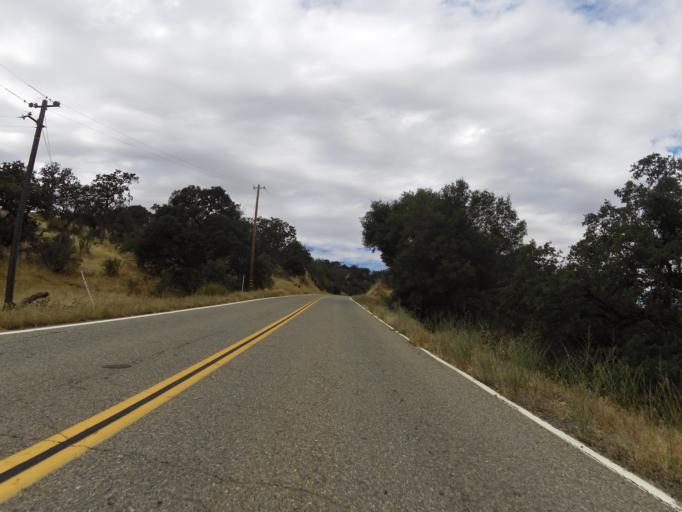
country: US
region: California
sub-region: Madera County
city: Yosemite Lakes
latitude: 37.2399
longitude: -119.7858
